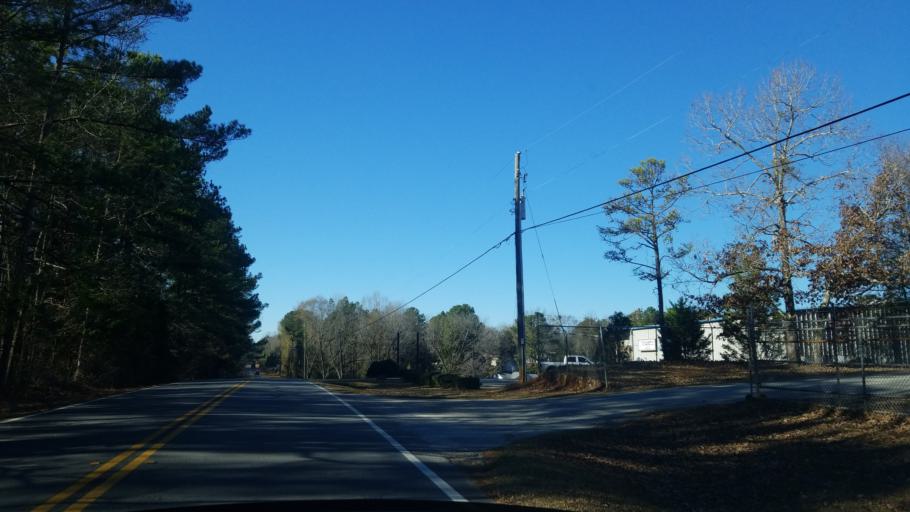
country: US
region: Georgia
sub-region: Harris County
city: Hamilton
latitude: 32.6650
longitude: -84.8704
